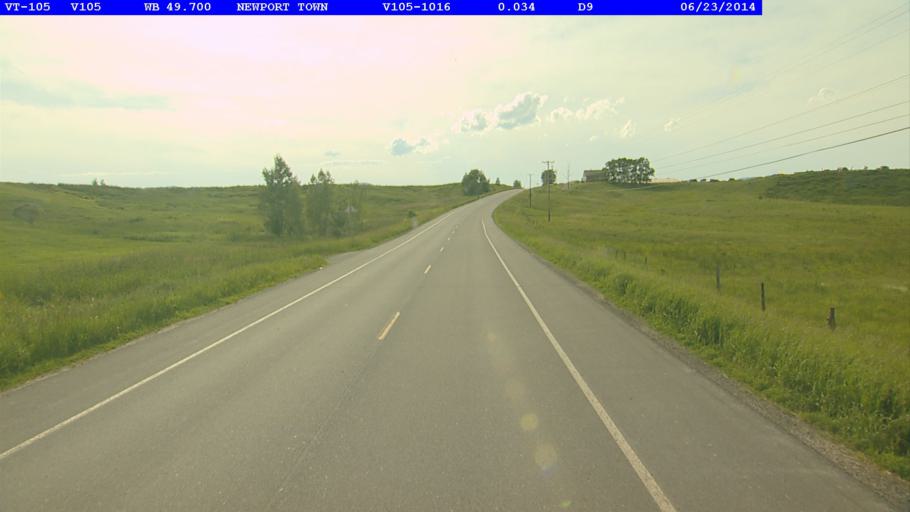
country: US
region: Vermont
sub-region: Orleans County
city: Newport
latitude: 44.9775
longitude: -72.3356
